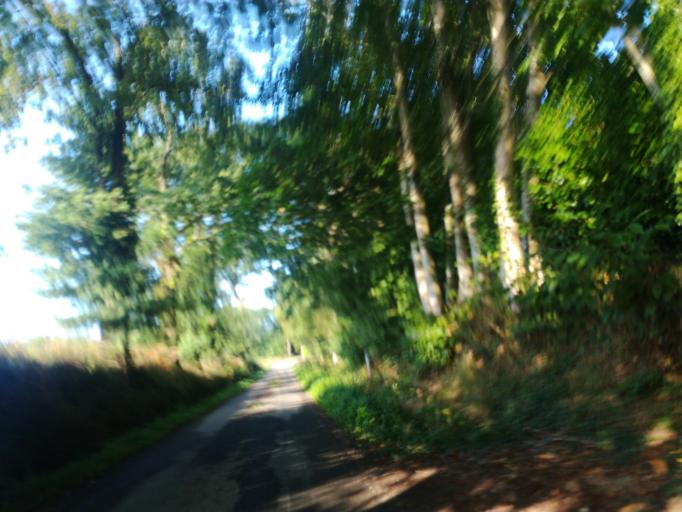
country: FR
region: Brittany
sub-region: Departement d'Ille-et-Vilaine
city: Fouillard
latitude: 48.1449
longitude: -1.5964
